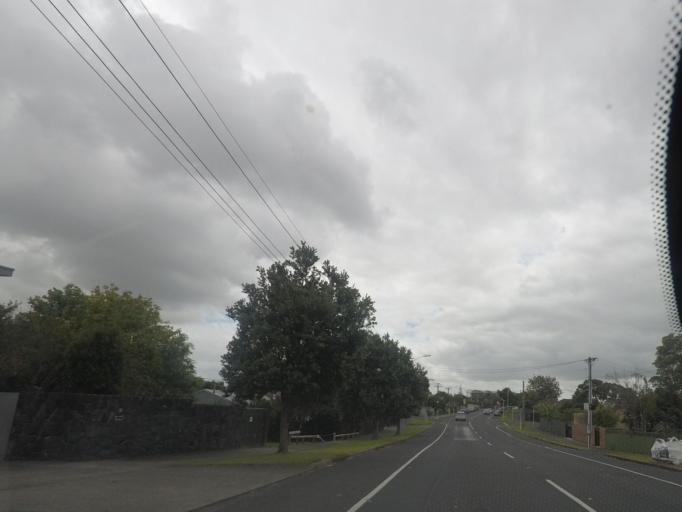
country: NZ
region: Auckland
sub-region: Auckland
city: Tamaki
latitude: -36.8701
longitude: 174.8632
